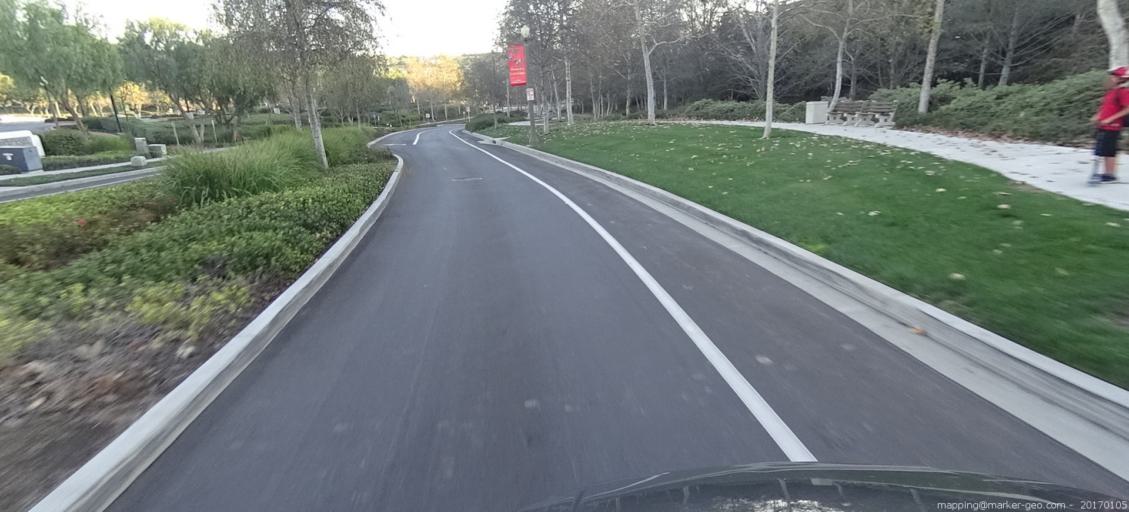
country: US
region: California
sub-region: Orange County
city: Ladera Ranch
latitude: 33.5442
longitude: -117.6406
